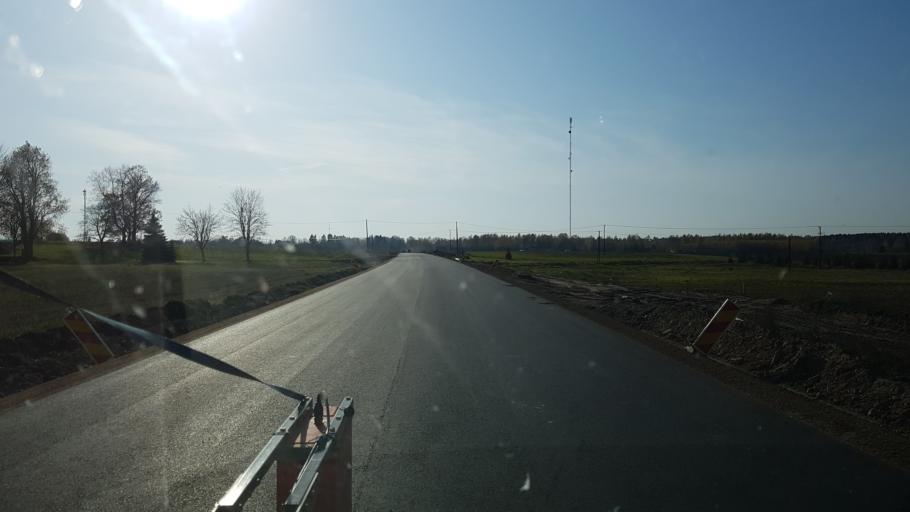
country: EE
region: Vorumaa
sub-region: Antsla vald
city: Vana-Antsla
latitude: 57.8404
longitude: 26.5499
